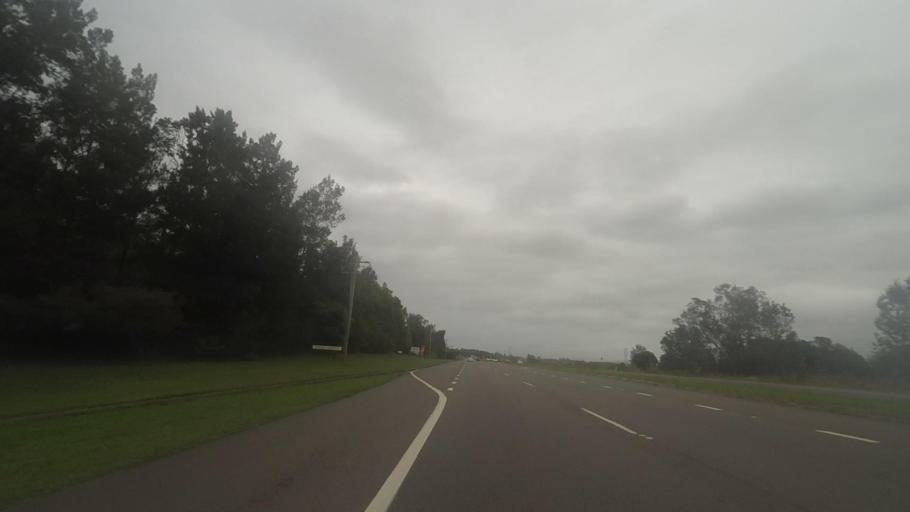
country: AU
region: New South Wales
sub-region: Port Stephens Shire
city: Raymond Terrace
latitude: -32.8005
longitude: 151.7162
